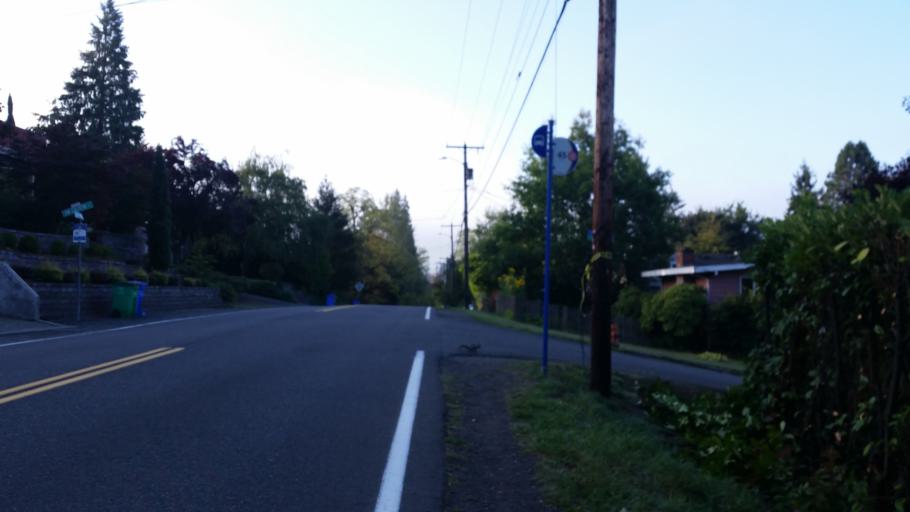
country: US
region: Oregon
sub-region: Washington County
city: Garden Home-Whitford
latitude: 45.4718
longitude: -122.7130
